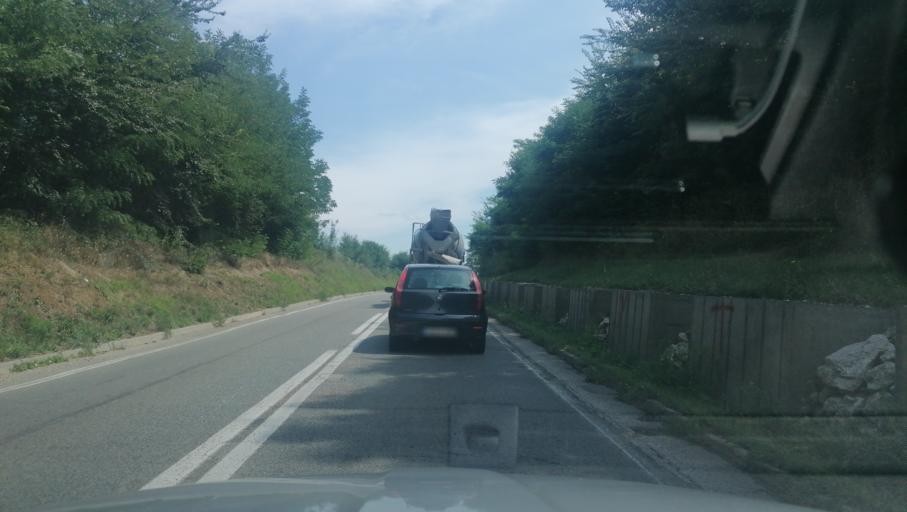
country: BA
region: Republika Srpska
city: Velika Obarska
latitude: 44.7695
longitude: 19.1275
